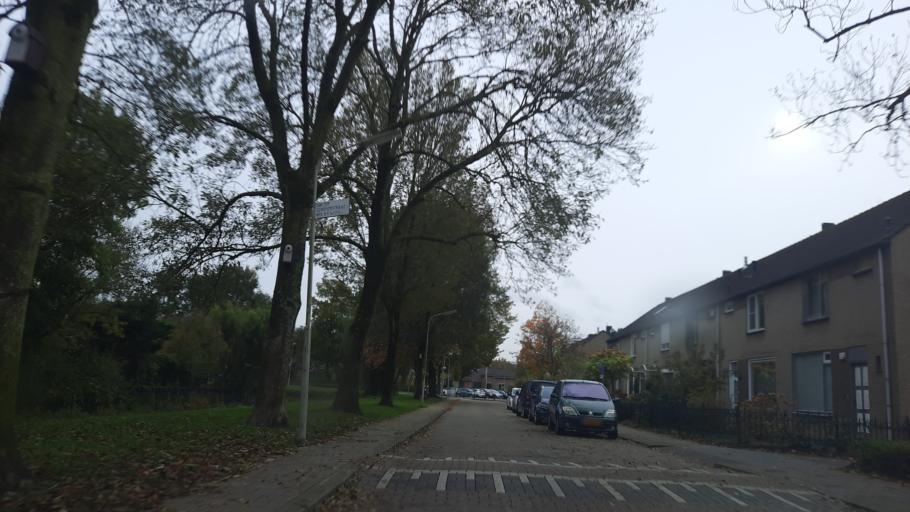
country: NL
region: South Holland
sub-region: Gemeente Gorinchem
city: Gorinchem
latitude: 51.8439
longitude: 4.9579
